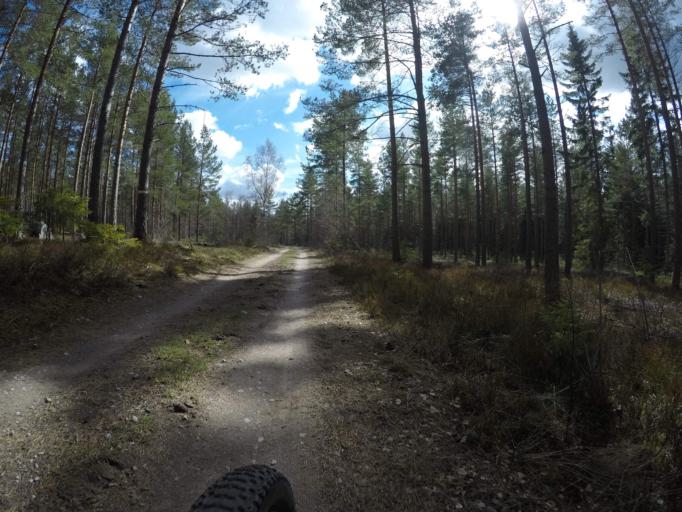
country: SE
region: Vaestmanland
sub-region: Kungsors Kommun
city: Kungsoer
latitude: 59.3597
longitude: 16.1092
